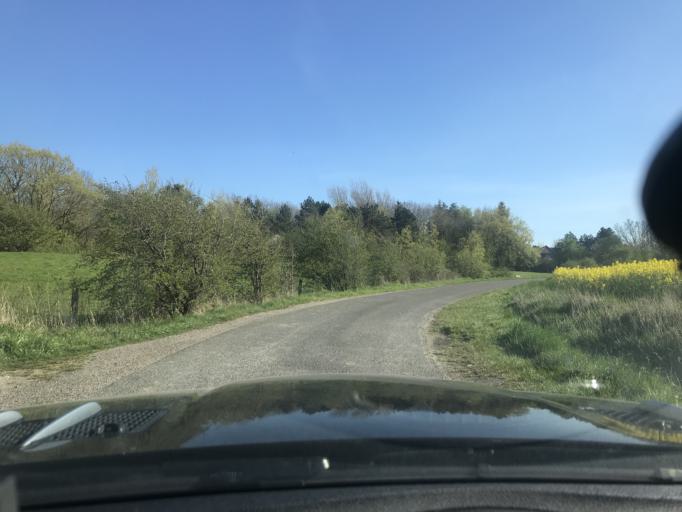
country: DE
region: Schleswig-Holstein
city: Grossenbrode
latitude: 54.4629
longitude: 11.0227
